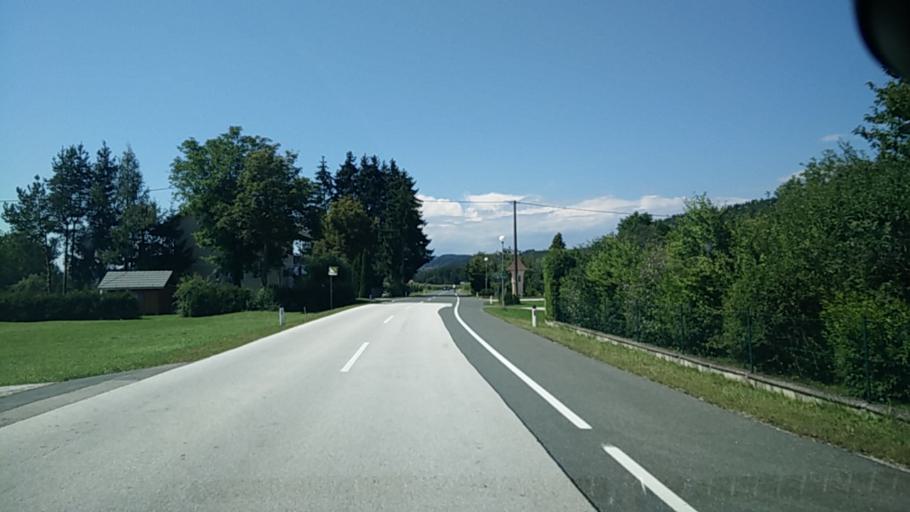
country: AT
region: Carinthia
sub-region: Politischer Bezirk Volkermarkt
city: Sittersdorf
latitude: 46.5499
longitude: 14.5849
